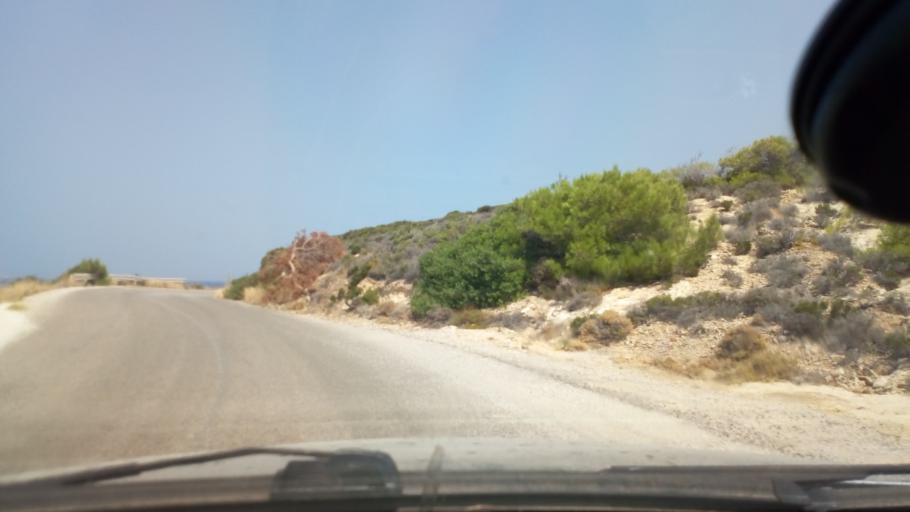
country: GR
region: North Aegean
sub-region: Nomos Samou
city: Agios Kirykos
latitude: 37.6324
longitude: 26.1149
